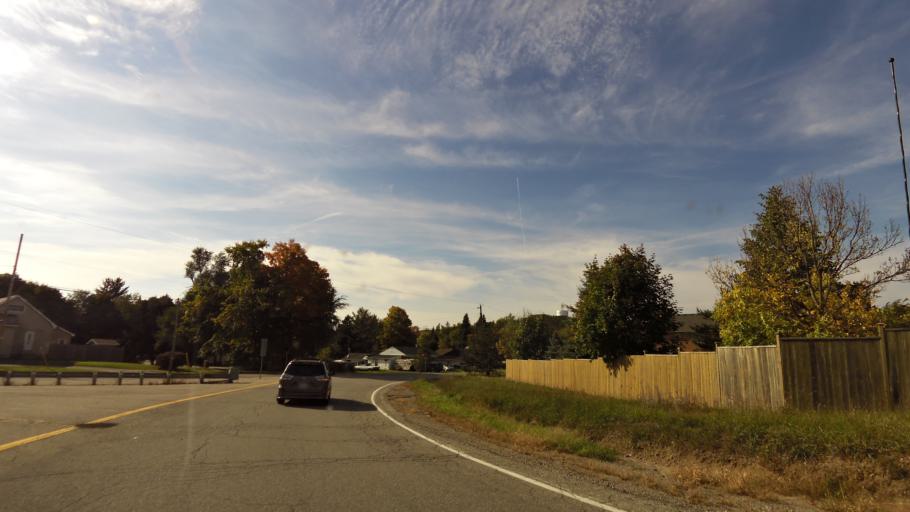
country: CA
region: Ontario
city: Orangeville
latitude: 43.7633
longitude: -80.0538
